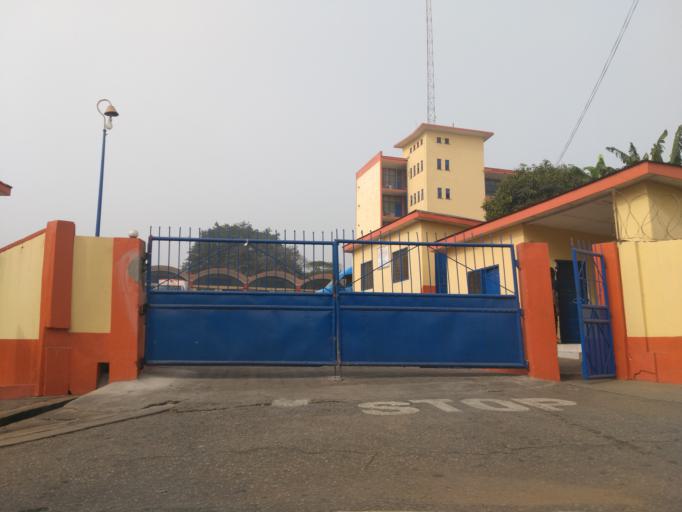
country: GH
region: Ashanti
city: Kumasi
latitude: 6.6911
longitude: -1.6229
